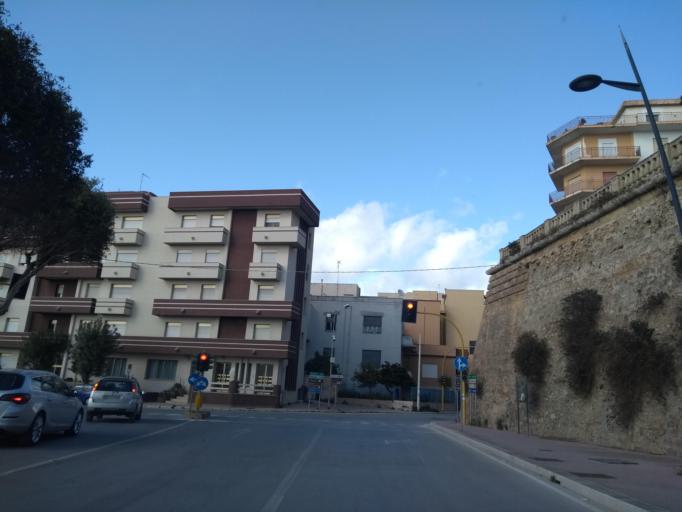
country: IT
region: Sicily
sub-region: Trapani
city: Marsala
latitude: 37.8043
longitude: 12.4339
